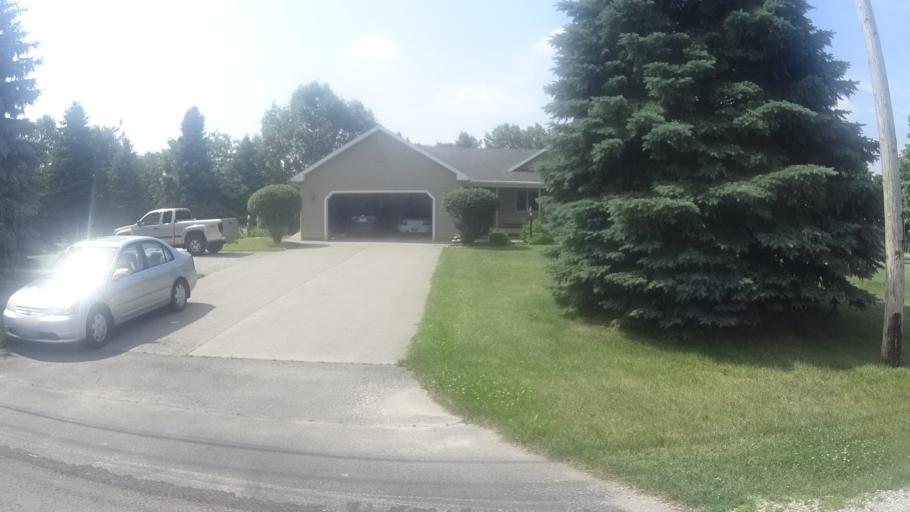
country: US
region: Ohio
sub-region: Erie County
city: Sandusky
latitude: 41.3551
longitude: -82.7269
